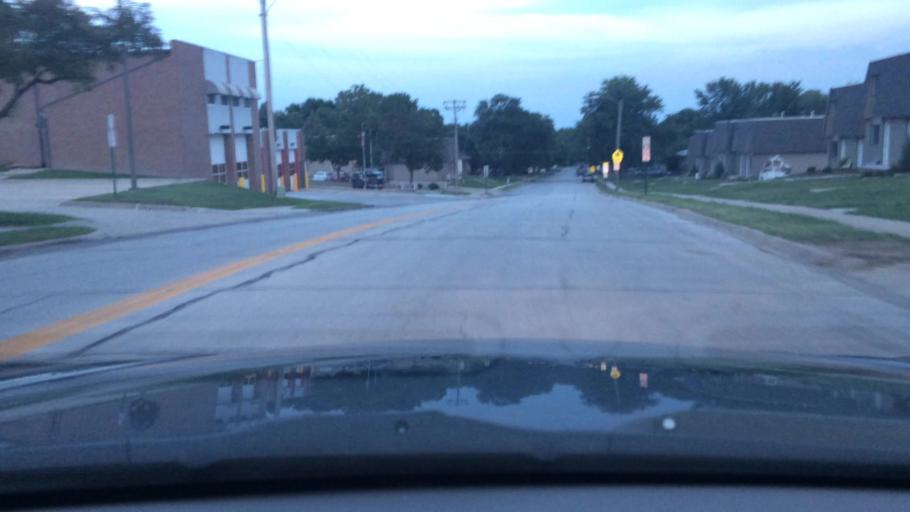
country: US
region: Nebraska
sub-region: Sarpy County
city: La Vista
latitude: 41.1874
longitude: -96.0398
